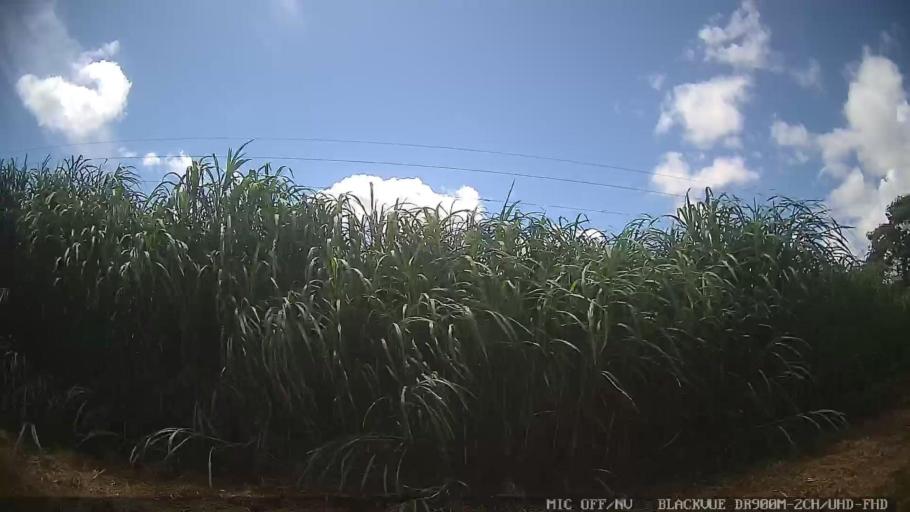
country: BR
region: Sao Paulo
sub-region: Amparo
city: Amparo
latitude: -22.8285
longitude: -46.7016
